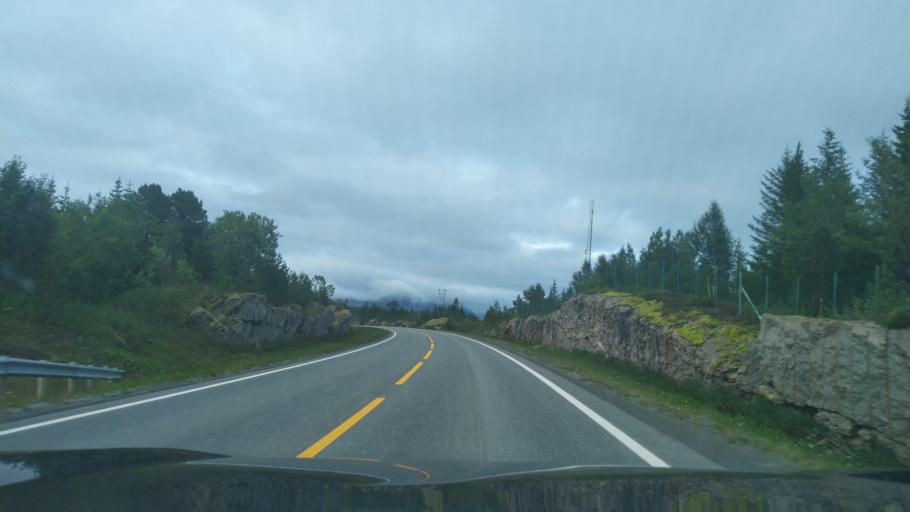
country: NO
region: Nordland
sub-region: Narvik
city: Narvik
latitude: 68.5224
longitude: 17.3897
